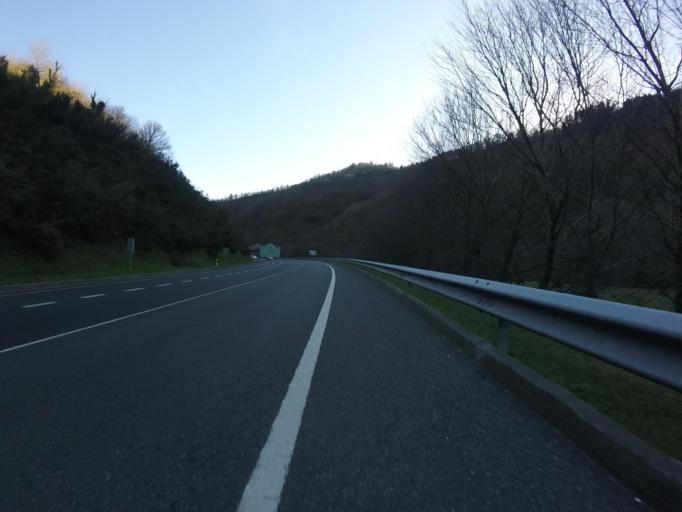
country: ES
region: Navarre
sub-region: Provincia de Navarra
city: Bera
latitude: 43.2633
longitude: -1.6855
